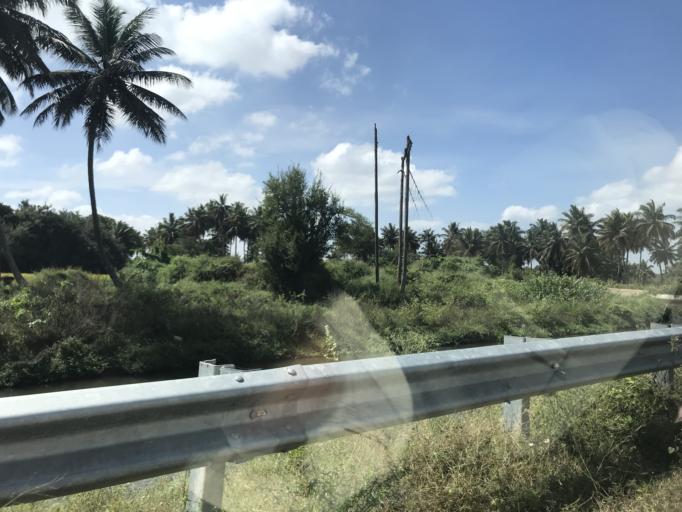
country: IN
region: Karnataka
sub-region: Mandya
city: Shrirangapattana
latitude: 12.4192
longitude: 76.6594
